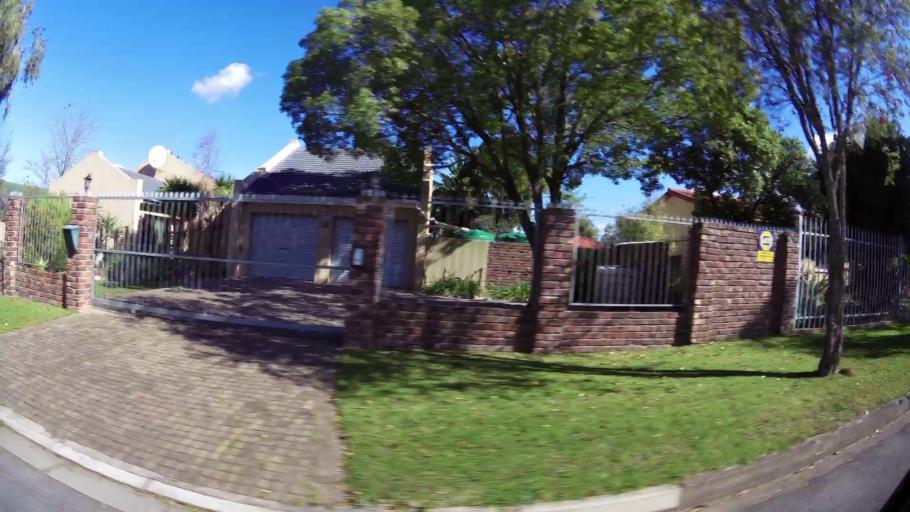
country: ZA
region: Western Cape
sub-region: Eden District Municipality
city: George
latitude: -33.9554
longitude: 22.4294
